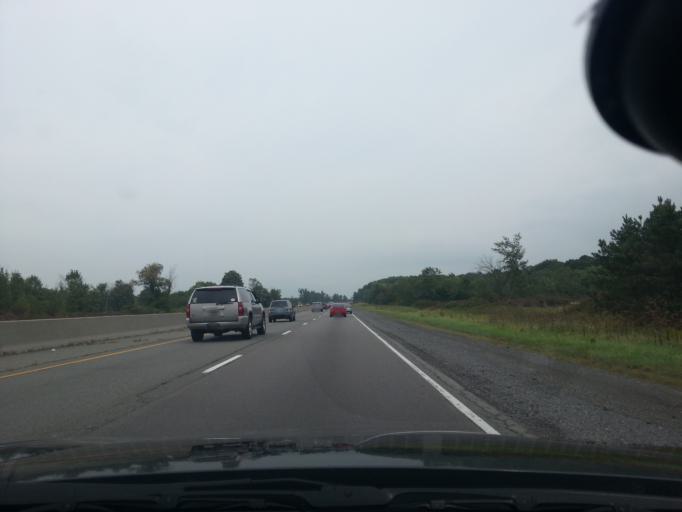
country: CA
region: Ontario
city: Kingston
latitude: 44.3103
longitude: -76.3939
